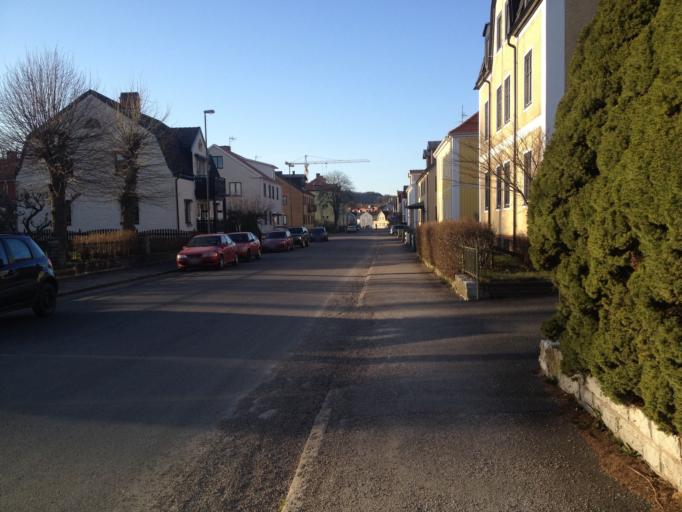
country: SE
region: Vaestra Goetaland
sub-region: Falkopings Kommun
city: Falkoeping
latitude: 58.1702
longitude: 13.5549
